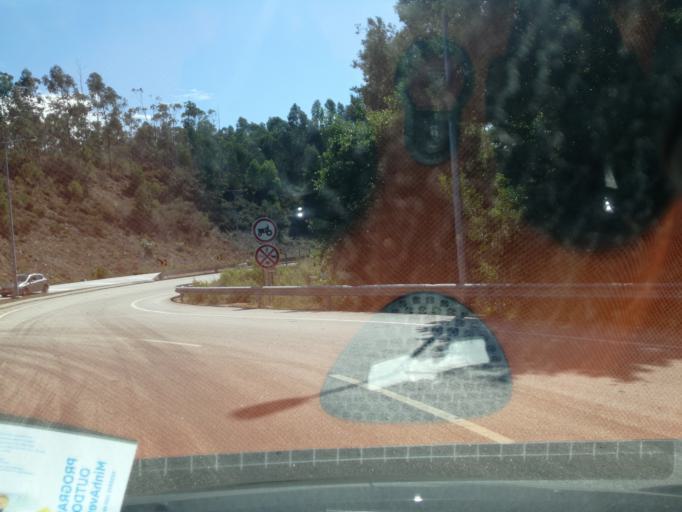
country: ES
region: Galicia
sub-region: Provincia de Pontevedra
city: O Rosal
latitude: 41.8808
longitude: -8.7958
